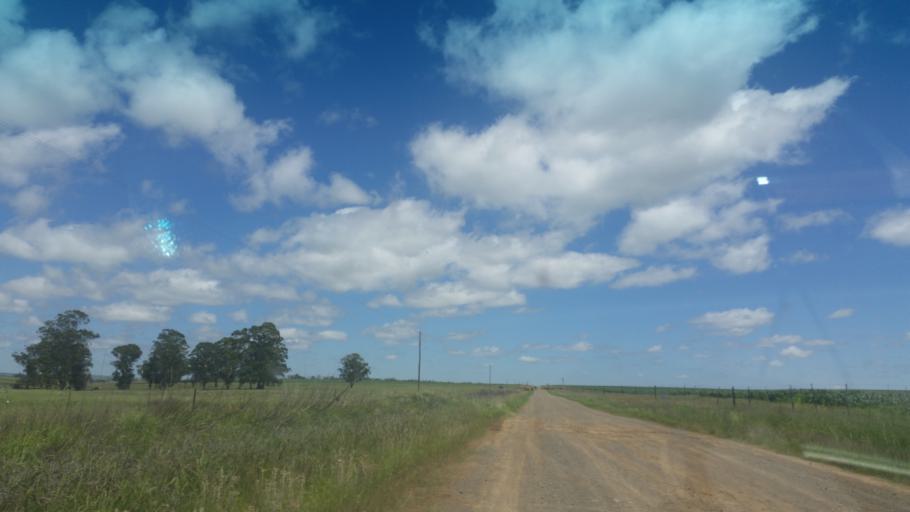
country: ZA
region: Orange Free State
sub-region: Thabo Mofutsanyana District Municipality
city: Harrismith
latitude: -28.1755
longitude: 29.0168
